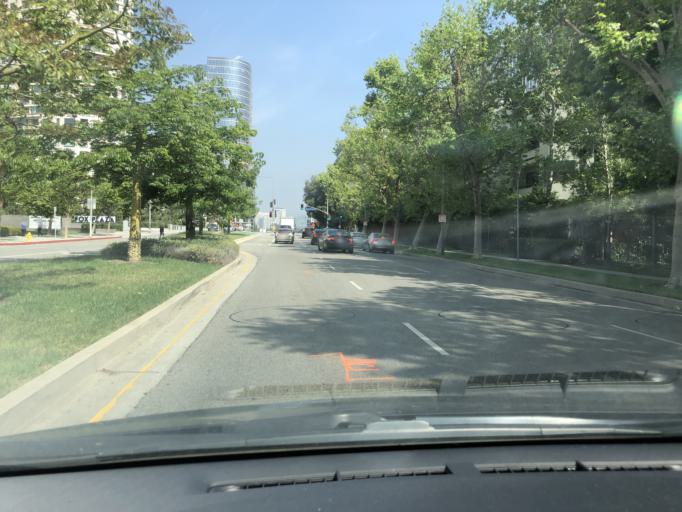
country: US
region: California
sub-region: Los Angeles County
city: Century City
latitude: 34.0554
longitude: -118.4126
